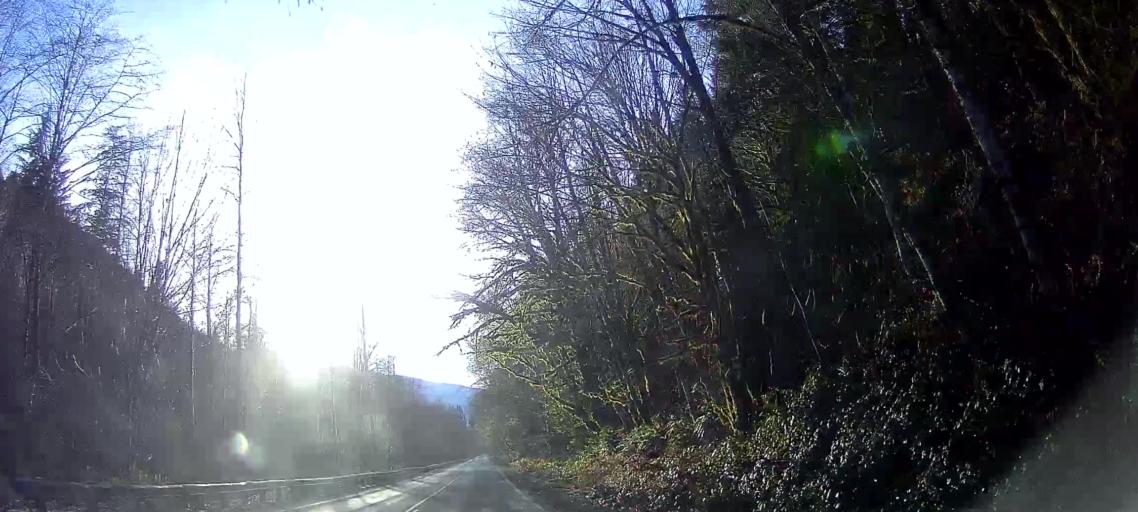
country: US
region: Washington
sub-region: Snohomish County
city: Darrington
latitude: 48.5604
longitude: -121.8394
